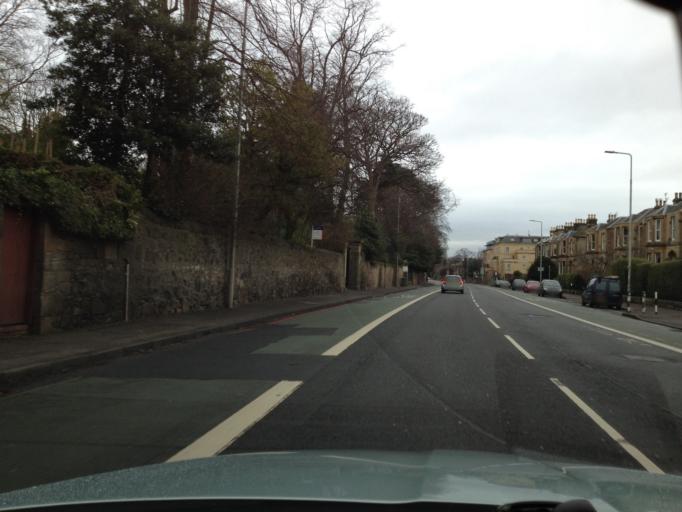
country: GB
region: Scotland
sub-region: Edinburgh
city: Colinton
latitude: 55.9452
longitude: -3.2479
